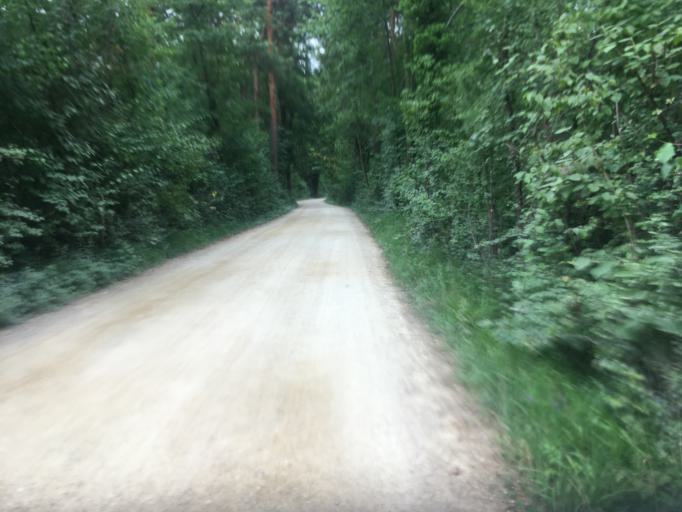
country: CH
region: Bern
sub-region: Jura bernois
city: La Neuveville
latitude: 47.0672
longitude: 7.1376
